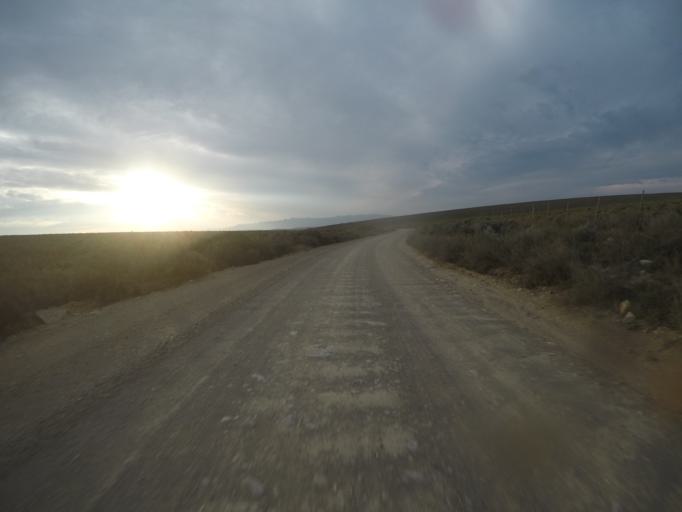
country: ZA
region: Eastern Cape
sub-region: Cacadu District Municipality
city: Willowmore
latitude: -33.5819
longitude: 23.1808
